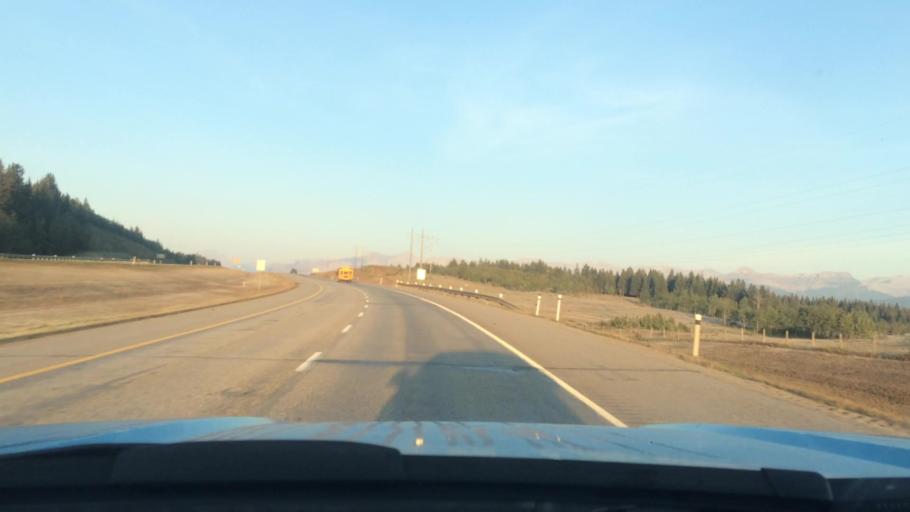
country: CA
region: Alberta
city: Cochrane
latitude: 51.1462
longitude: -114.8633
